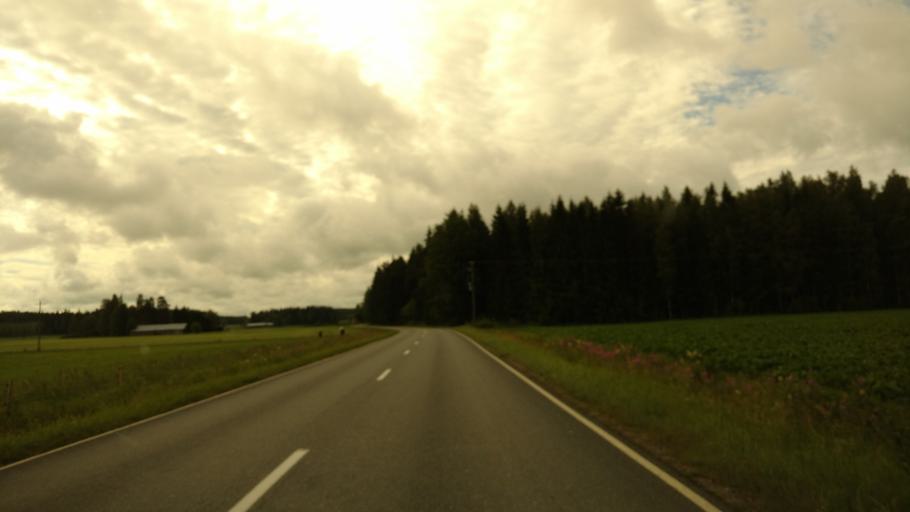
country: FI
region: Varsinais-Suomi
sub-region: Loimaa
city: Koski Tl
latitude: 60.5983
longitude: 23.1274
